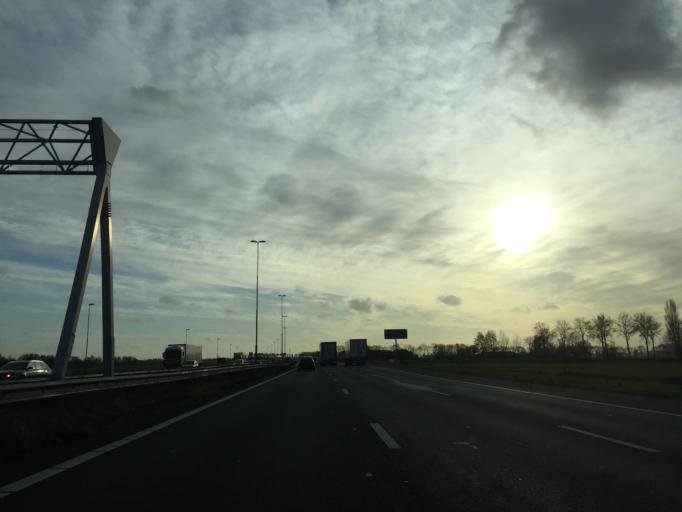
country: NL
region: Gelderland
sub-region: Gemeente Zaltbommel
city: Zaltbommel
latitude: 51.7884
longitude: 5.2578
